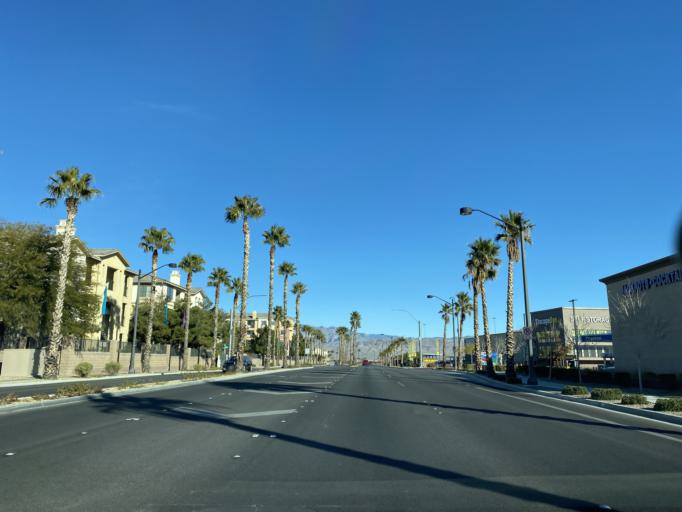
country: US
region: Nevada
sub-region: Clark County
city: Summerlin South
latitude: 36.2967
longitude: -115.2897
